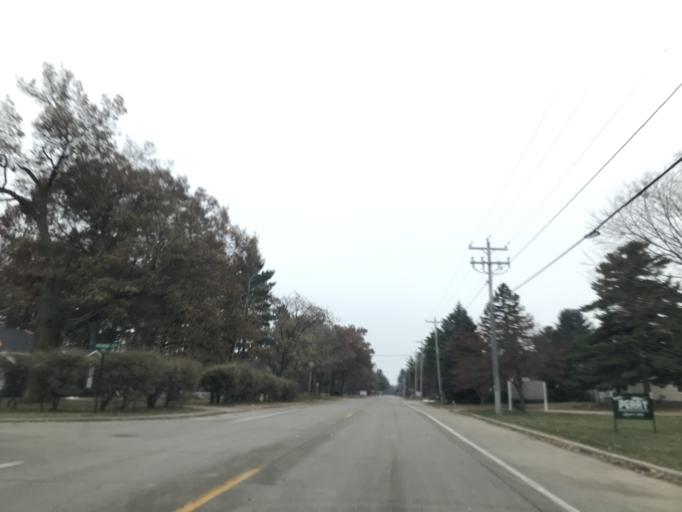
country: US
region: Wisconsin
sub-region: Marinette County
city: Marinette
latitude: 45.0743
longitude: -87.6194
